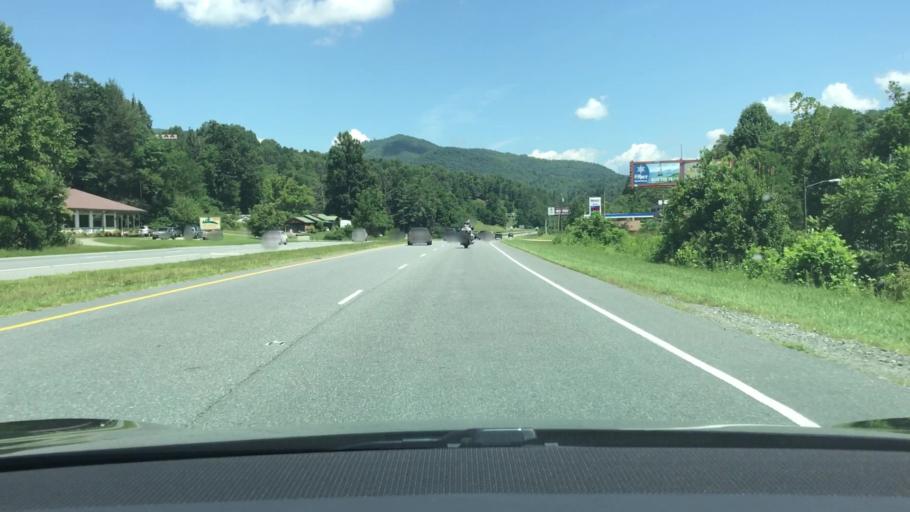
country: US
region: North Carolina
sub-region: Jackson County
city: Sylva
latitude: 35.3163
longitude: -83.2616
